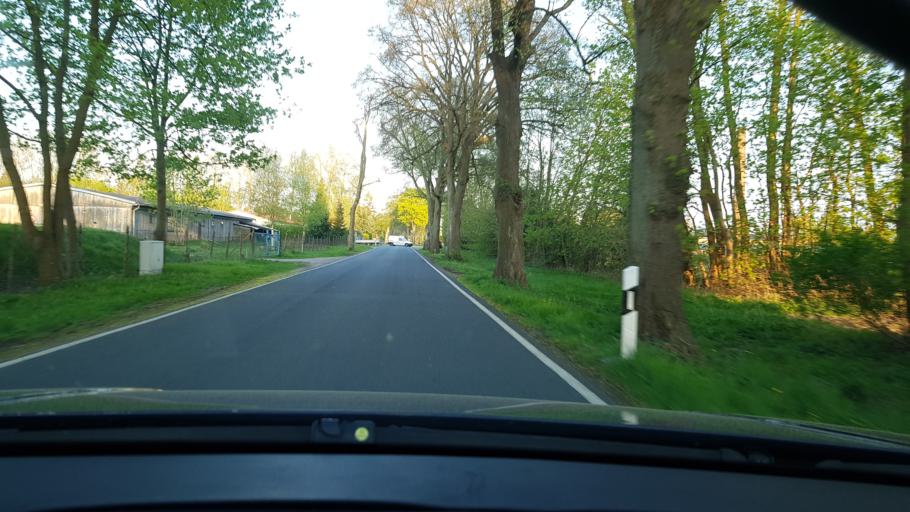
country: DE
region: Mecklenburg-Vorpommern
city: Alt-Sanitz
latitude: 53.8954
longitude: 13.5871
